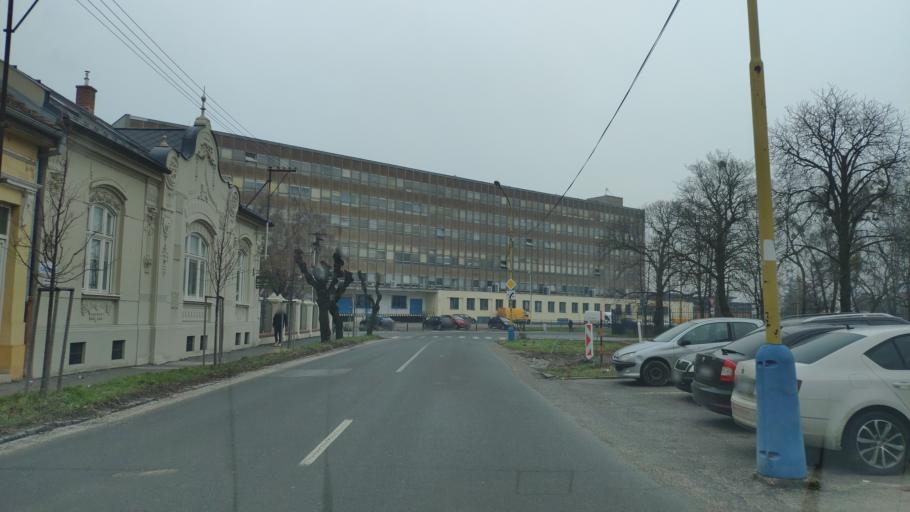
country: SK
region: Kosicky
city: Kosice
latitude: 48.7261
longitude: 21.2651
